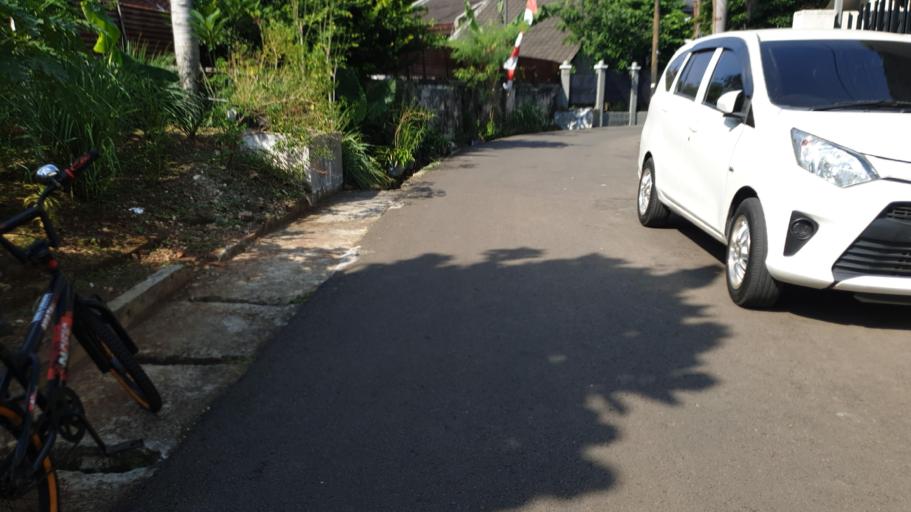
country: ID
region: Jakarta Raya
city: Jakarta
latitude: -6.2937
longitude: 106.8385
